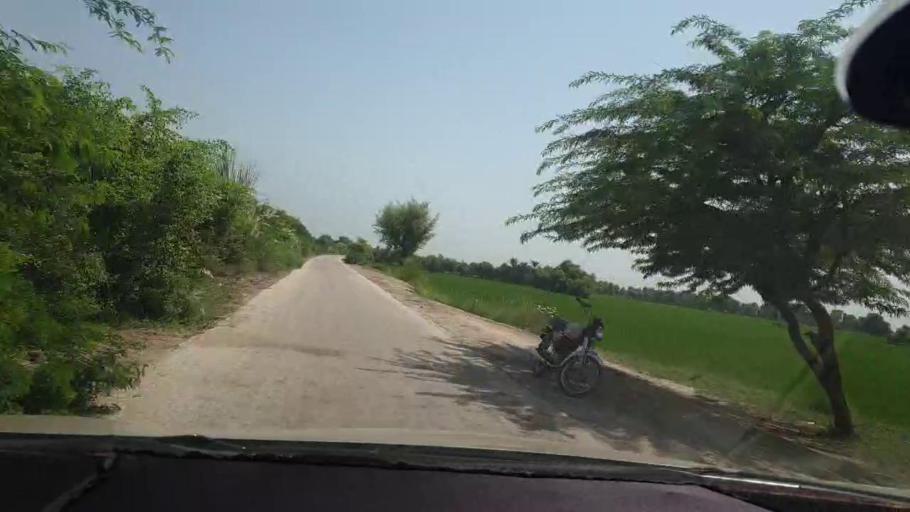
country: PK
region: Sindh
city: Kambar
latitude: 27.5150
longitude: 68.0109
